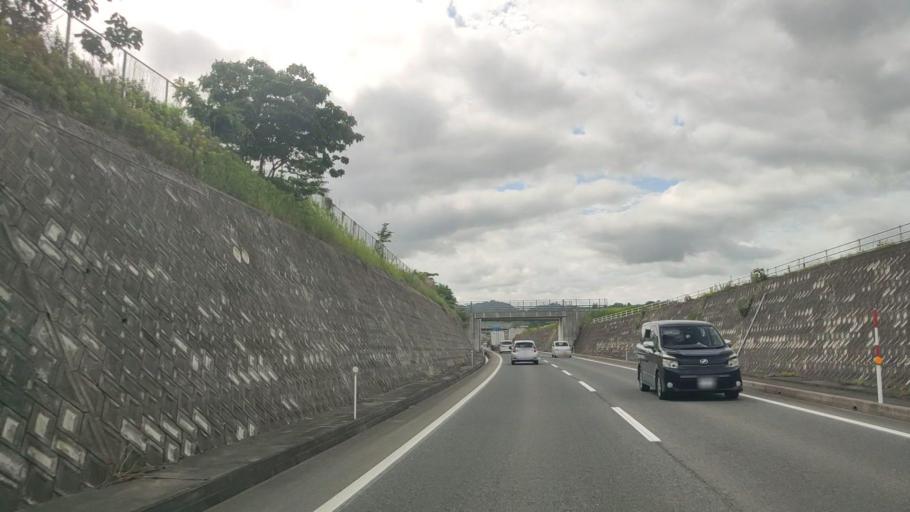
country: JP
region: Tottori
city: Yonago
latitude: 35.3865
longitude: 133.3846
